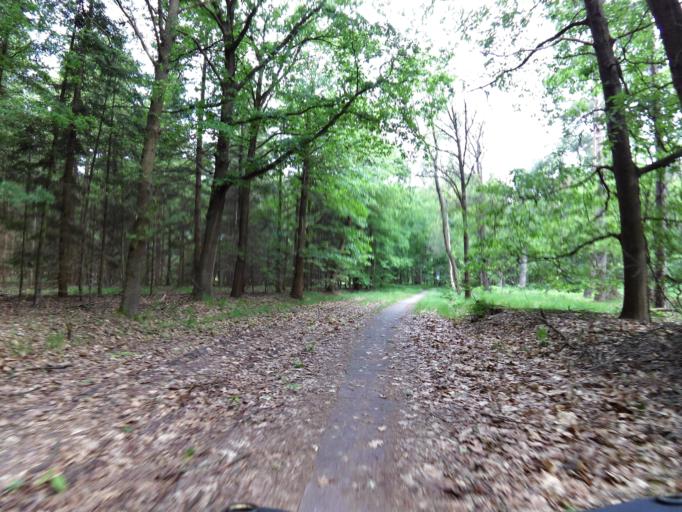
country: NL
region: North Brabant
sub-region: Gemeente Baarle-Nassau
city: Baarle-Nassau
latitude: 51.5213
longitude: 4.8869
